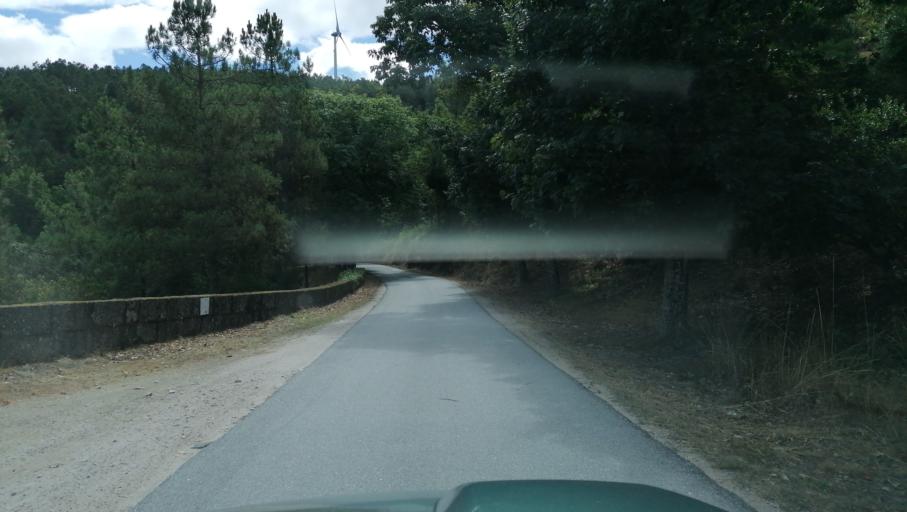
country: PT
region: Vila Real
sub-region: Vila Pouca de Aguiar
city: Vila Pouca de Aguiar
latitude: 41.5323
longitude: -7.5975
